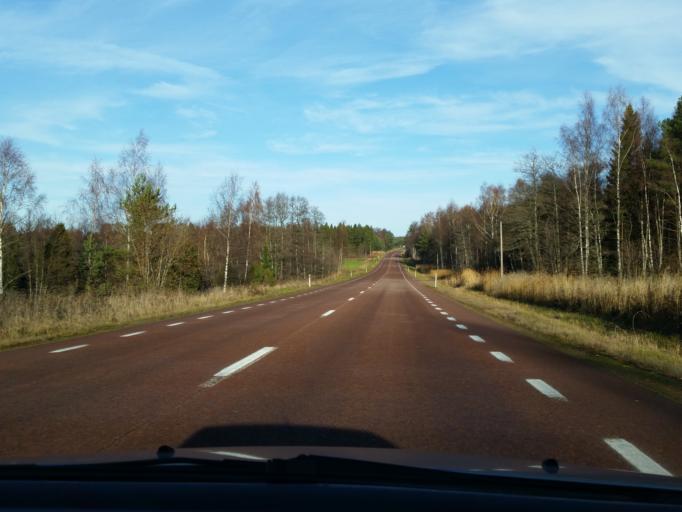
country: AX
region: Alands landsbygd
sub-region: Finstroem
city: Finstroem
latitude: 60.2961
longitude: 19.9531
